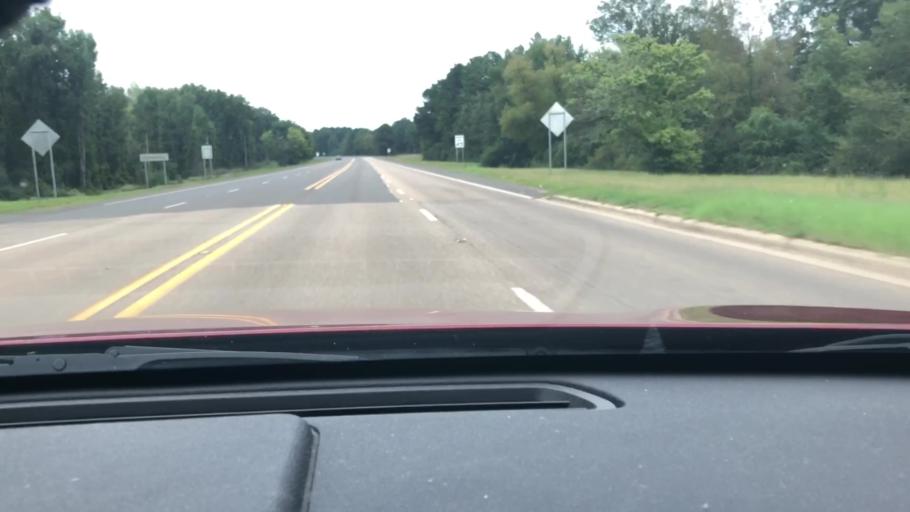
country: US
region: Arkansas
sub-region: Lafayette County
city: Lewisville
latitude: 33.3552
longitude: -93.5749
